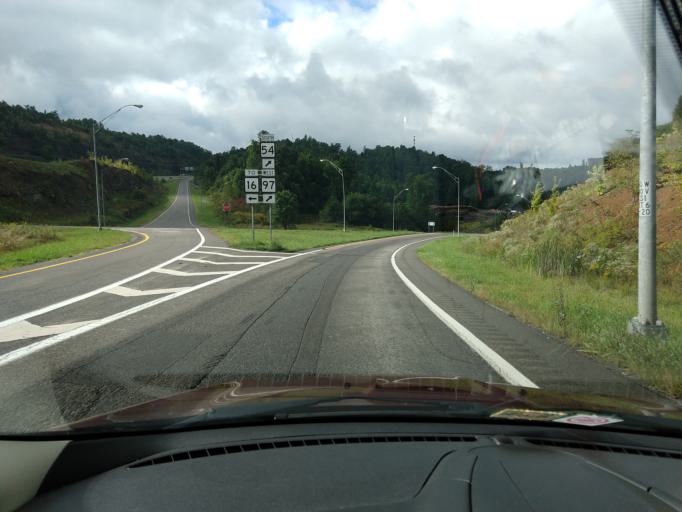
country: US
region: West Virginia
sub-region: Raleigh County
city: Sophia
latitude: 37.7198
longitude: -81.2547
